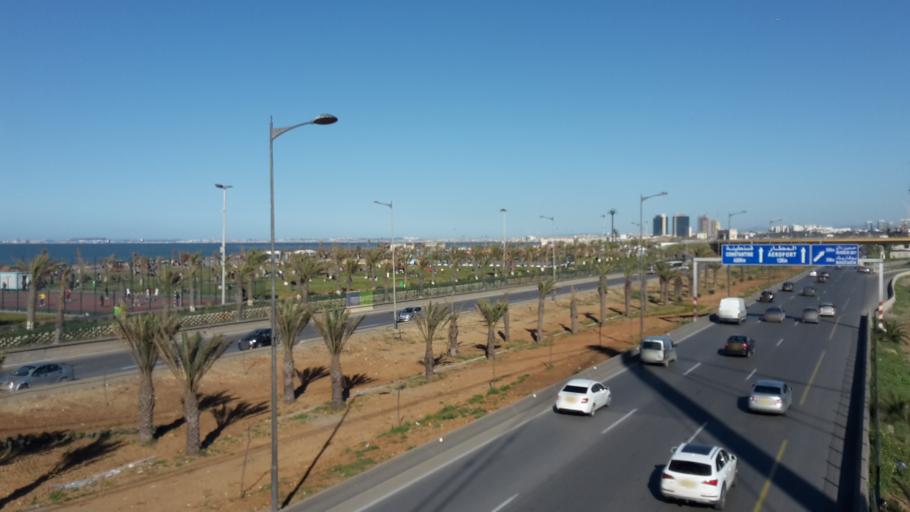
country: DZ
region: Alger
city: Bab Ezzouar
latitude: 36.7411
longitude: 3.1183
